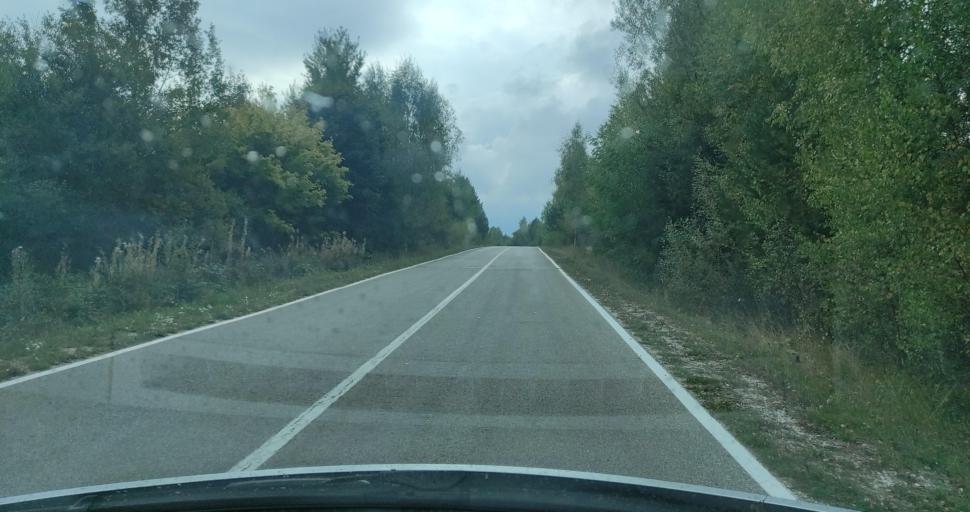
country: RS
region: Central Serbia
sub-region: Jablanicki Okrug
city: Crna Trava
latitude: 42.6924
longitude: 22.3193
